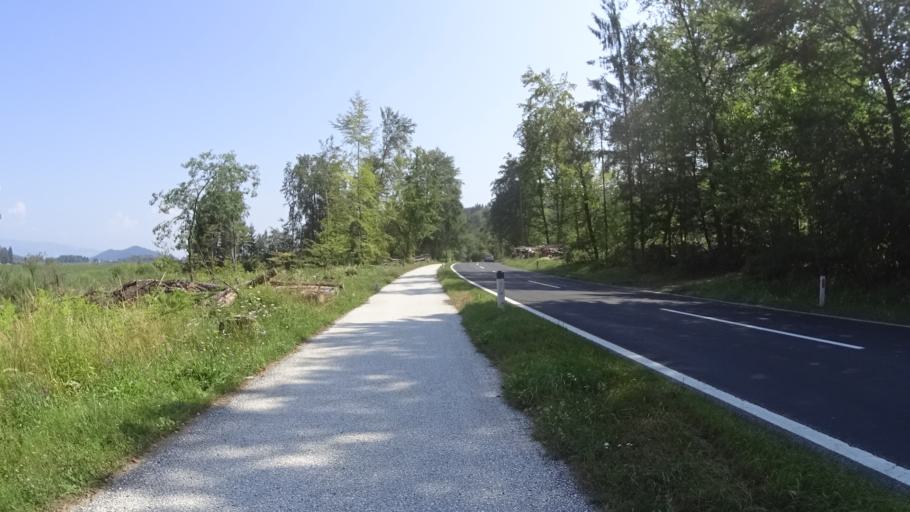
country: AT
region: Carinthia
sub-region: Politischer Bezirk Volkermarkt
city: Sittersdorf
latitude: 46.5566
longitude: 14.6180
